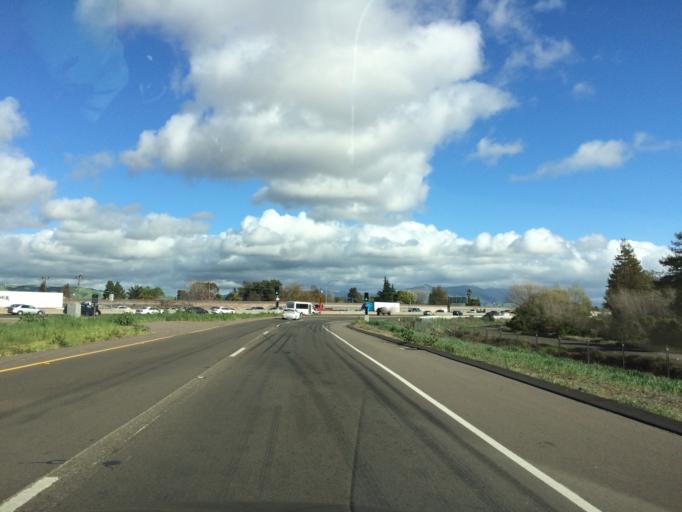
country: US
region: California
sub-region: Alameda County
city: Newark
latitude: 37.5620
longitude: -122.0385
